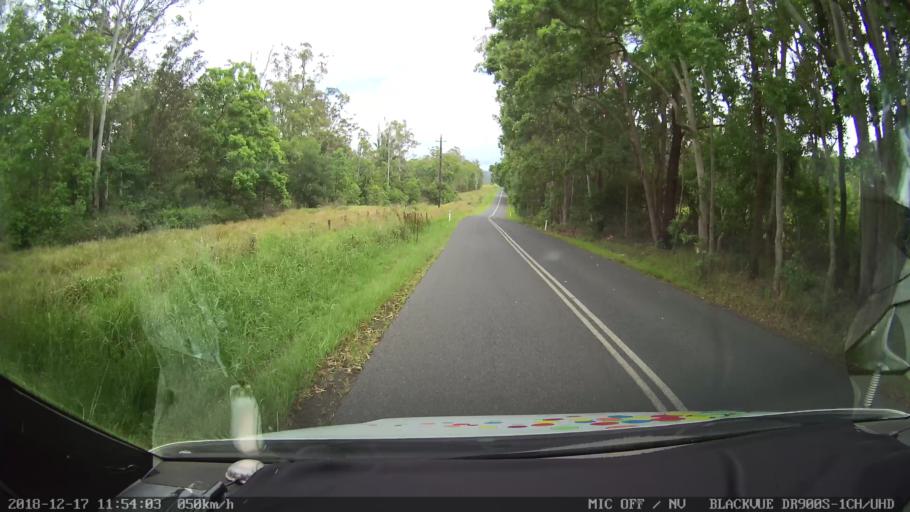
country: AU
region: New South Wales
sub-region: Kyogle
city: Kyogle
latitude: -28.5699
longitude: 152.5849
